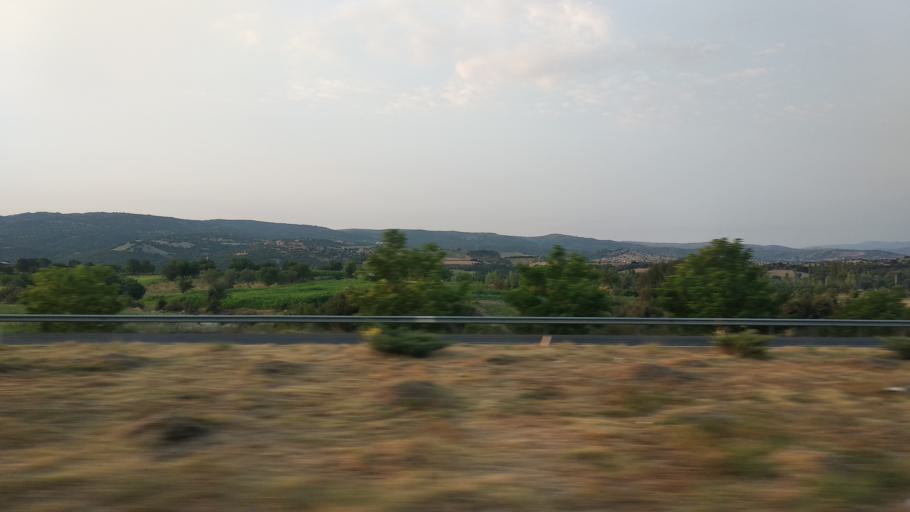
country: TR
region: Manisa
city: Selendi
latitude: 38.6218
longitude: 28.9213
